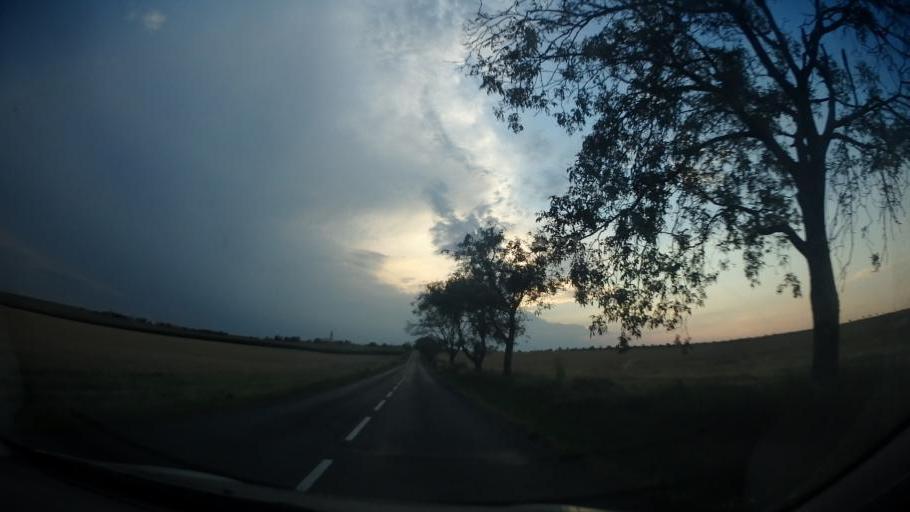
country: CZ
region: South Moravian
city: Orechov
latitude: 49.1103
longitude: 16.5377
